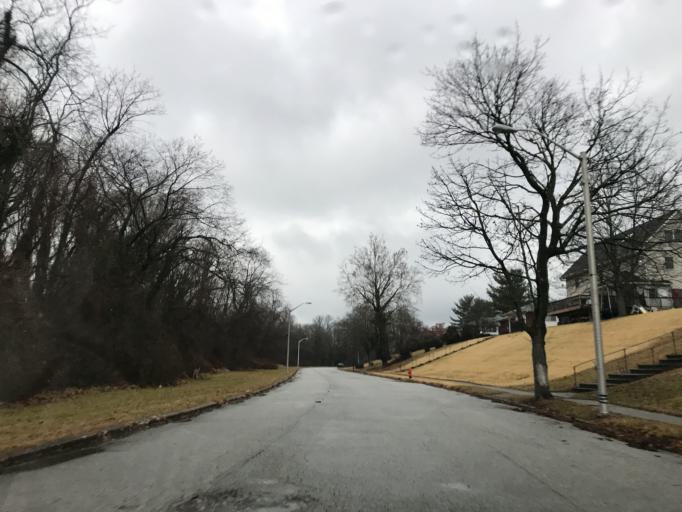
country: US
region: Maryland
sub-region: Baltimore County
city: Pikesville
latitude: 39.3703
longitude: -76.6738
